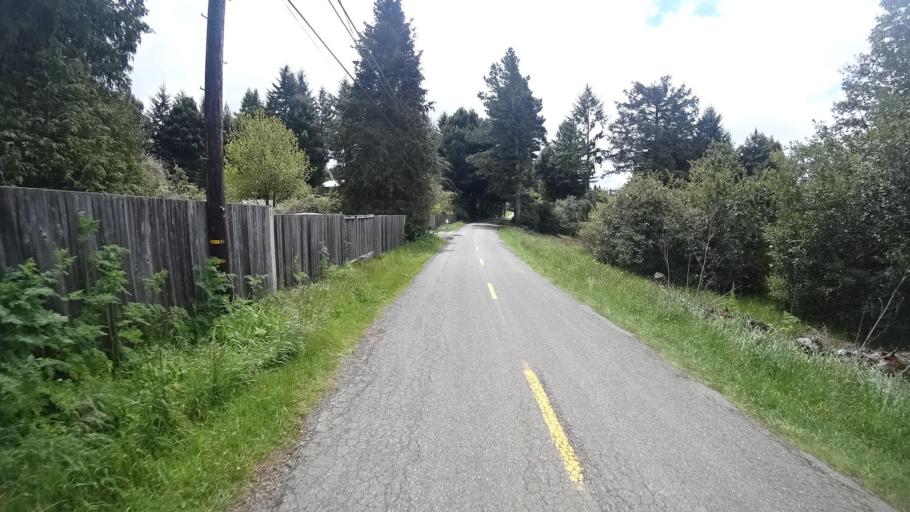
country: US
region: California
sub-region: Humboldt County
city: Bayside
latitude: 40.7686
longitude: -123.9994
